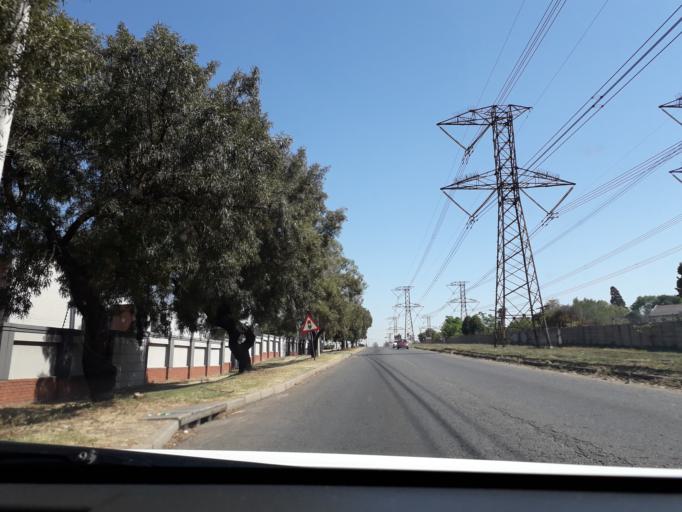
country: ZA
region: Gauteng
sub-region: City of Johannesburg Metropolitan Municipality
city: Modderfontein
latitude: -26.1292
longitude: 28.1889
